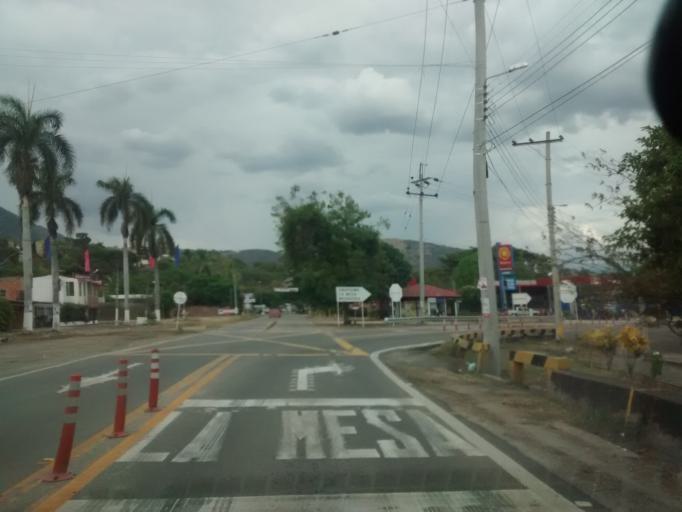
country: CO
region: Cundinamarca
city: Tocaima
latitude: 4.4552
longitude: -74.6447
